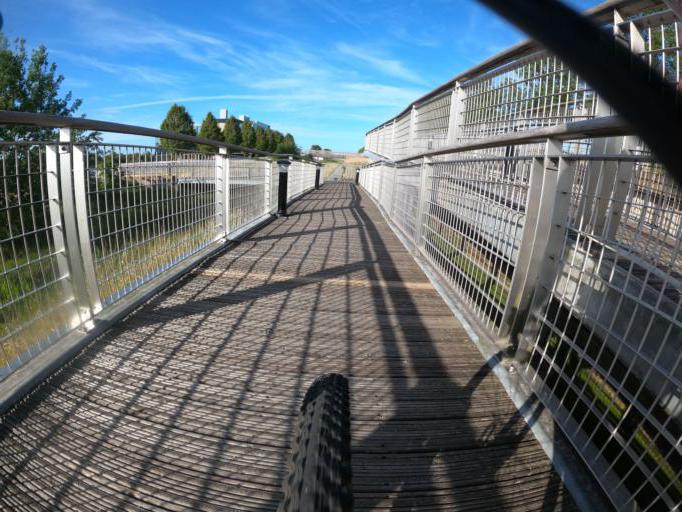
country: GB
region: Scotland
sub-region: Midlothian
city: Loanhead
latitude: 55.9194
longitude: -3.1317
